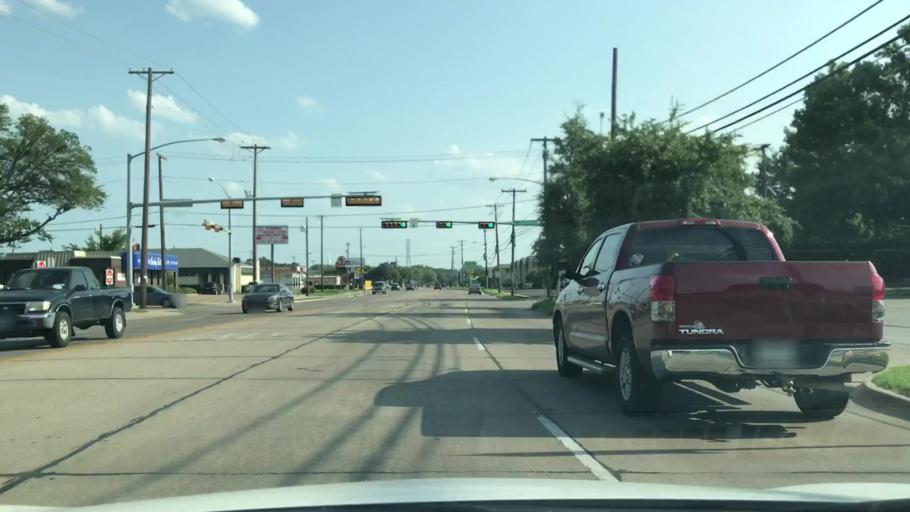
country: US
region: Texas
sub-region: Dallas County
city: Irving
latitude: 32.8217
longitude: -96.9496
